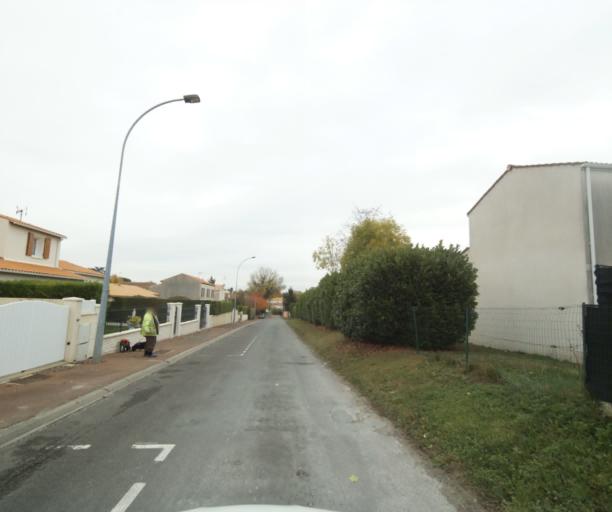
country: FR
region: Poitou-Charentes
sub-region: Departement de la Charente-Maritime
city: Saintes
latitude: 45.7435
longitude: -0.6573
